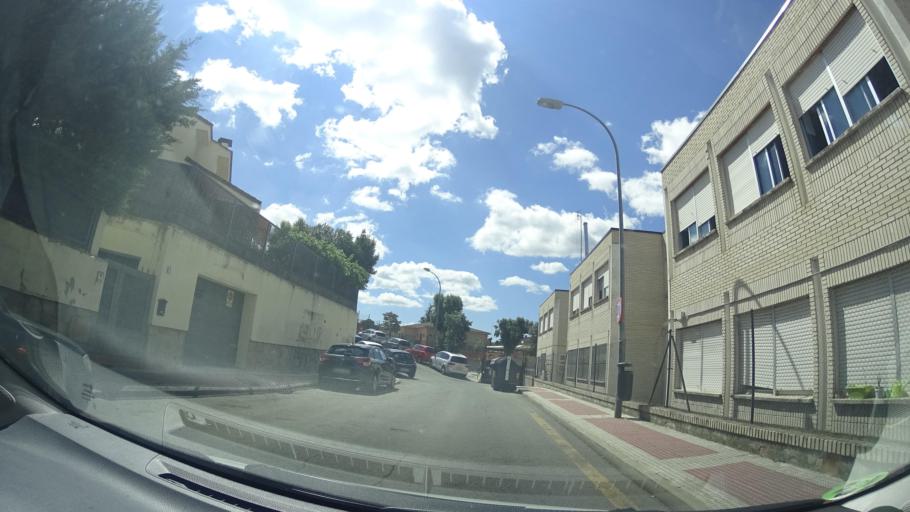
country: ES
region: Madrid
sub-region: Provincia de Madrid
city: Collado-Villalba
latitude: 40.6268
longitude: -4.0002
